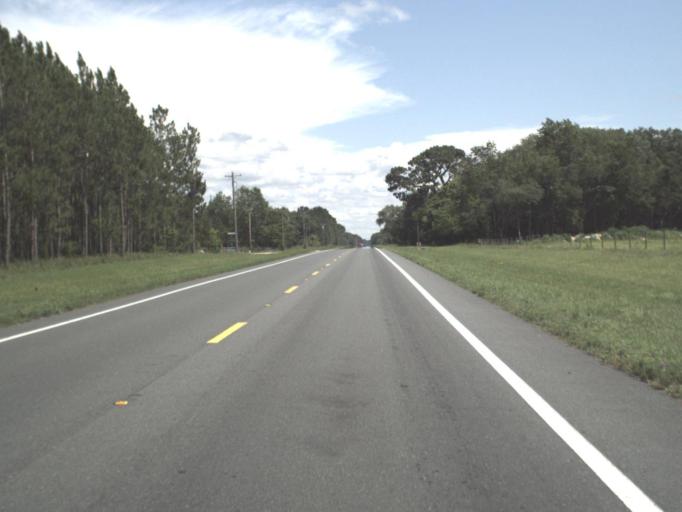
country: US
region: Florida
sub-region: Lafayette County
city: Mayo
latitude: 30.0810
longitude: -83.2165
